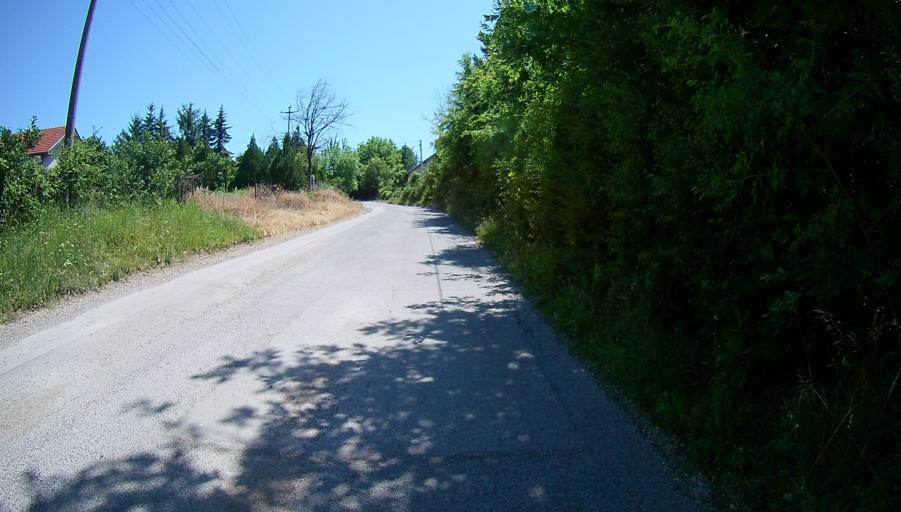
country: RS
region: Central Serbia
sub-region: Nisavski Okrug
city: Nis
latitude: 43.2932
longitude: 21.9000
